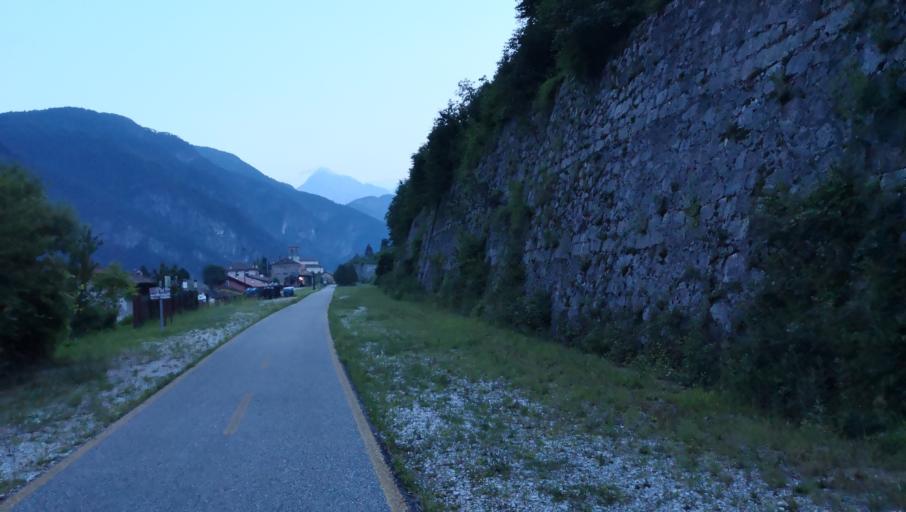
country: IT
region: Friuli Venezia Giulia
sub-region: Provincia di Udine
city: Chiusaforte
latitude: 46.4111
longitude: 13.3129
